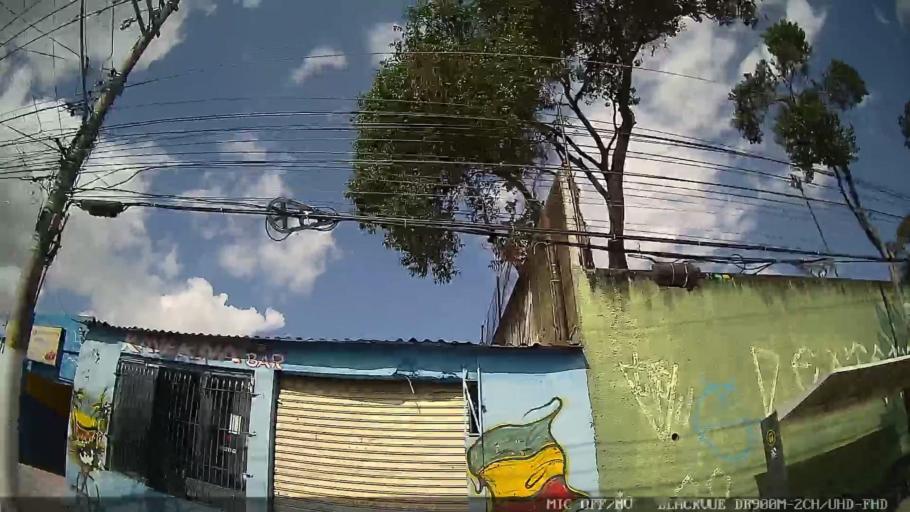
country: BR
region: Sao Paulo
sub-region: Guarulhos
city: Guarulhos
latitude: -23.5014
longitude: -46.4766
